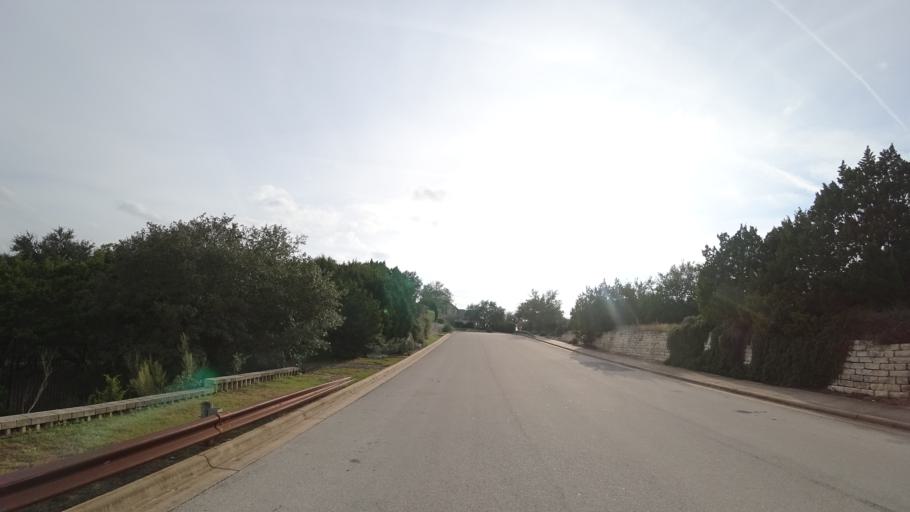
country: US
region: Texas
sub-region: Travis County
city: Hudson Bend
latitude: 30.3768
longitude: -97.8800
